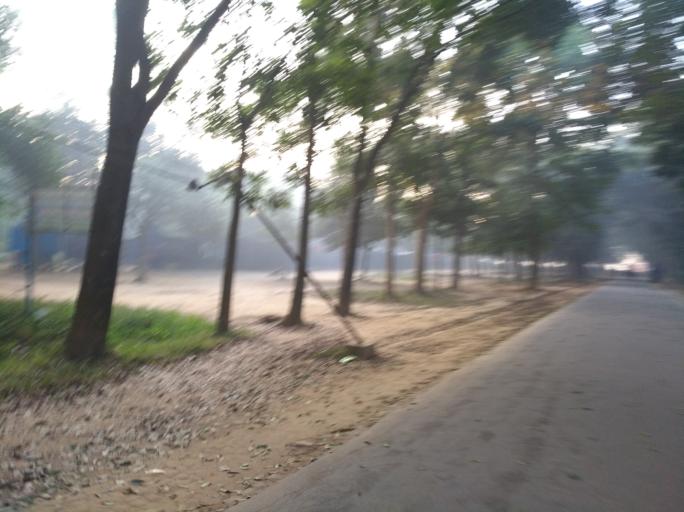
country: BD
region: Dhaka
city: Tungi
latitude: 23.8821
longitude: 90.2713
